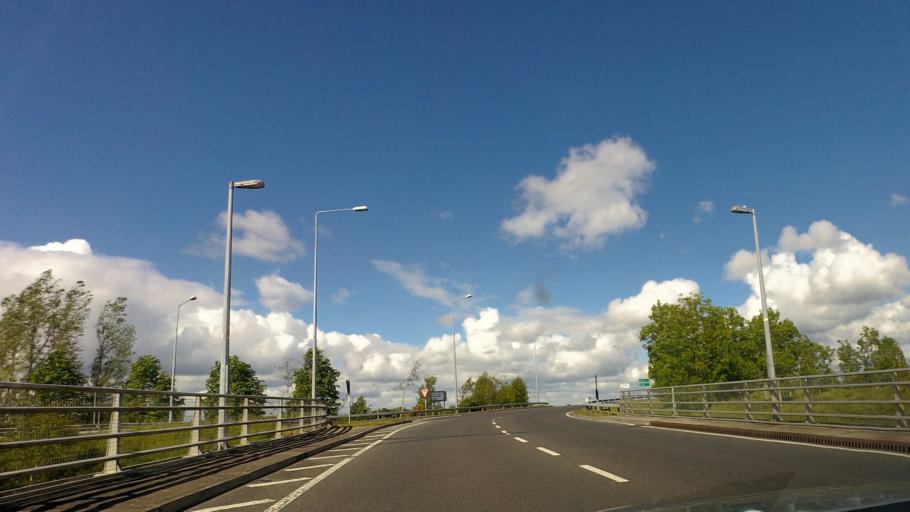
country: IE
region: Munster
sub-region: An Clar
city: Shannon
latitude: 52.7265
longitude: -8.8756
